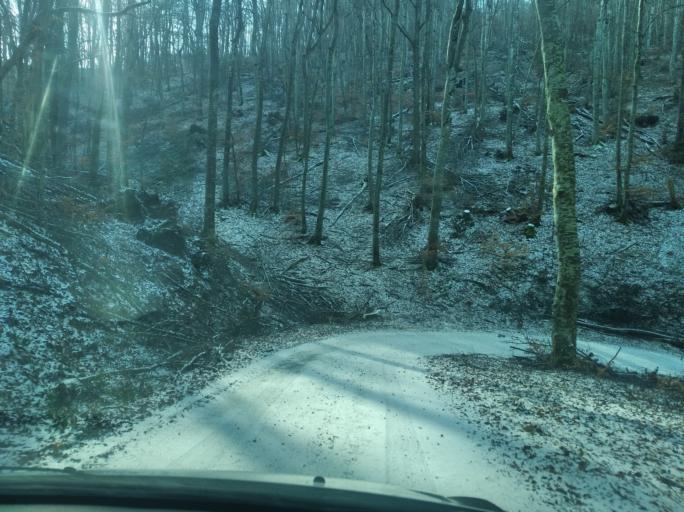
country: FR
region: Auvergne
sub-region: Departement de l'Allier
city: Le Mayet-de-Montagne
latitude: 46.1497
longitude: 3.7559
